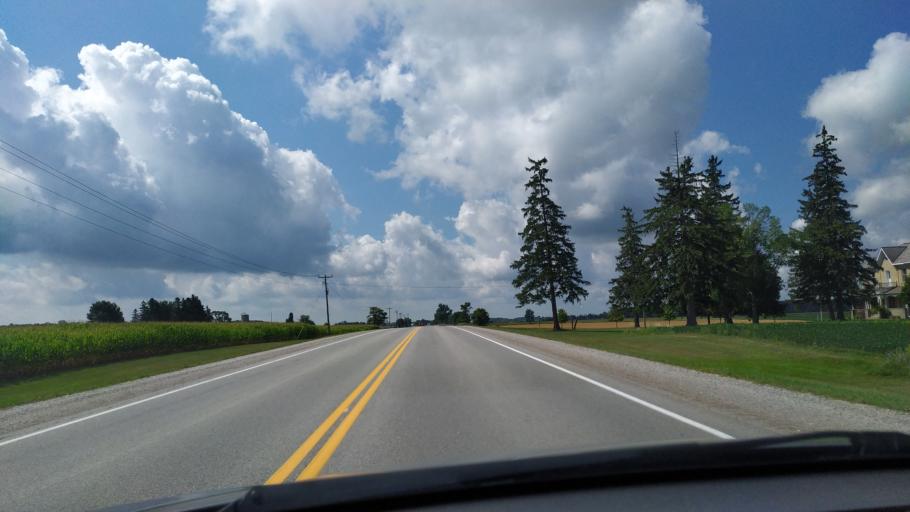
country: CA
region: Ontario
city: Huron East
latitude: 43.4091
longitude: -81.2481
